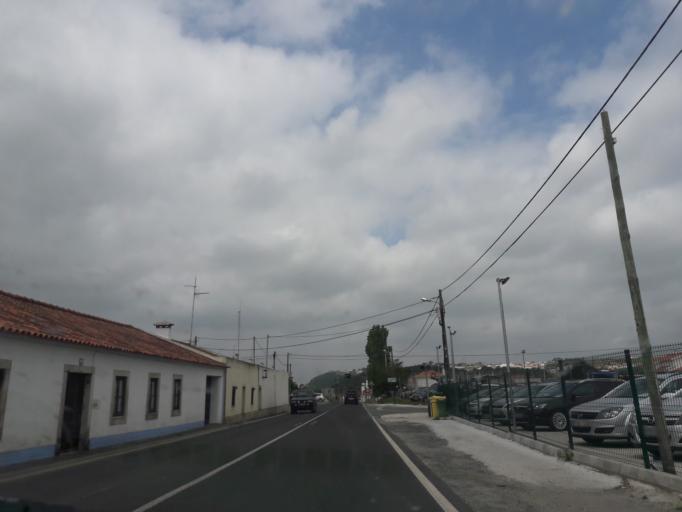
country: PT
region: Leiria
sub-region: Obidos
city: Obidos
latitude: 39.3440
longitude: -9.1675
